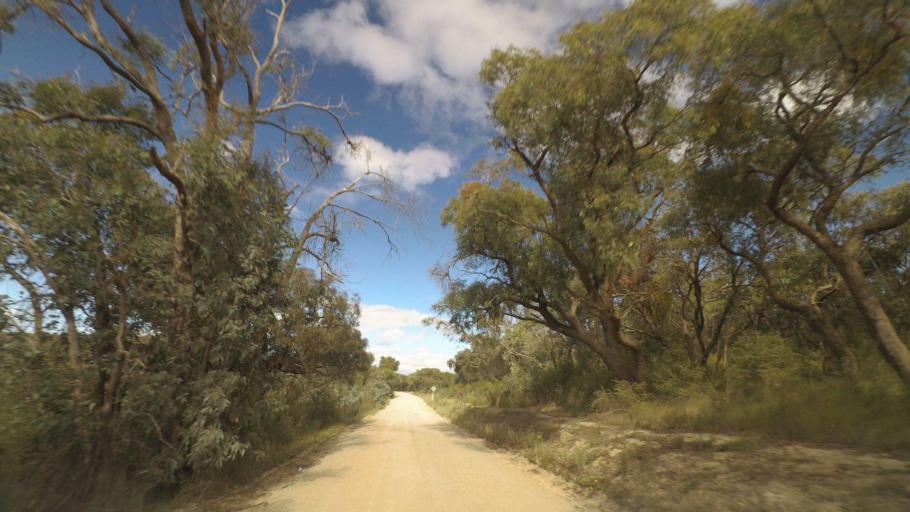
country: AU
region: Victoria
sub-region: Cardinia
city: Gembrook
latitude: -37.9939
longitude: 145.6131
